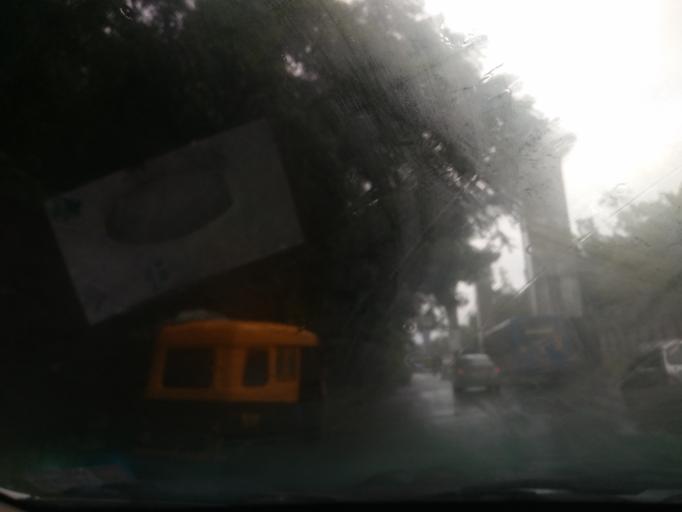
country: IN
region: Goa
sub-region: North Goa
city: Panaji
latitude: 15.5082
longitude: 73.8360
